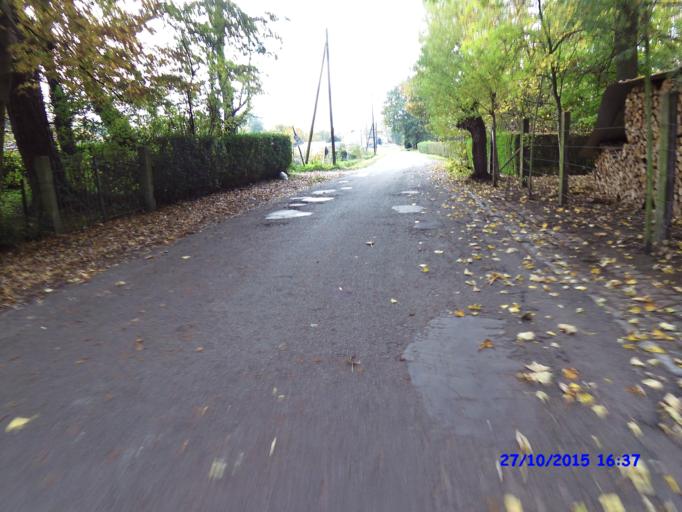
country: BE
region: Flanders
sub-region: Provincie Antwerpen
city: Brasschaat
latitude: 51.2670
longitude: 4.4570
